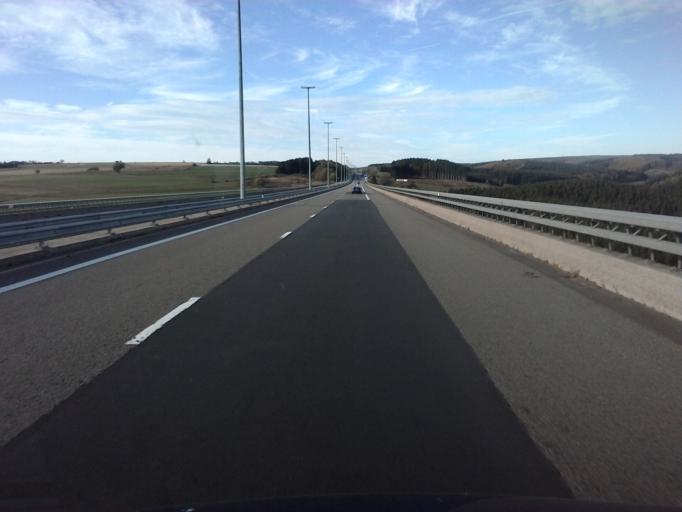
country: DE
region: Rheinland-Pfalz
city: Winterspelt
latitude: 50.2372
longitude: 6.1813
